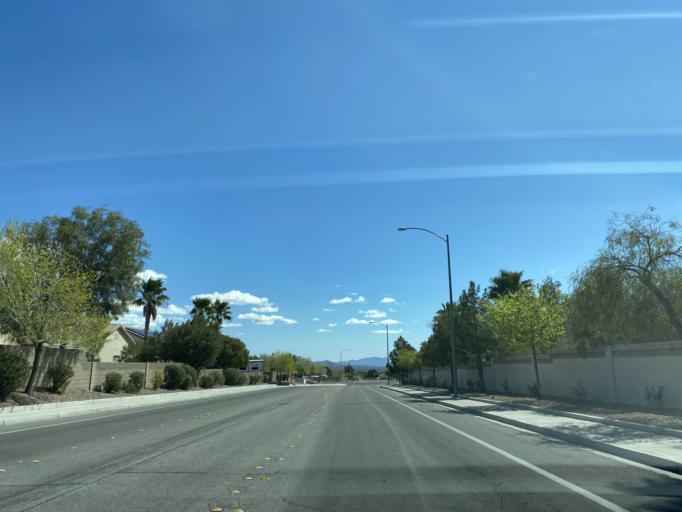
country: US
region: Nevada
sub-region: Clark County
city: Summerlin South
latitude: 36.3251
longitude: -115.2896
